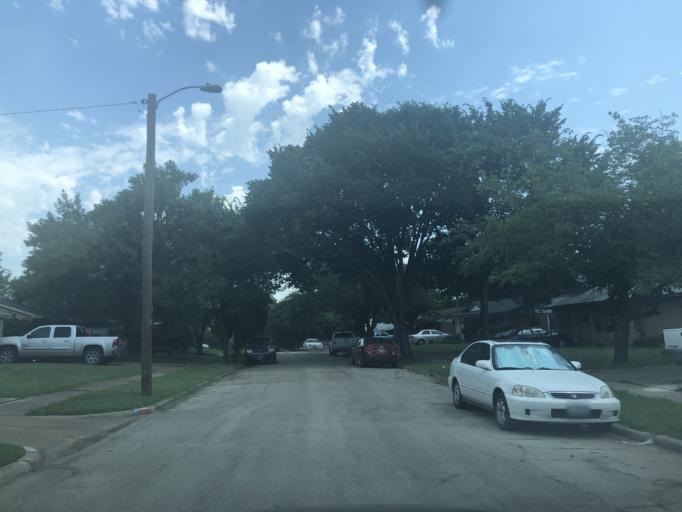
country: US
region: Texas
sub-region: Dallas County
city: Grand Prairie
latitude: 32.7222
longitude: -97.0120
